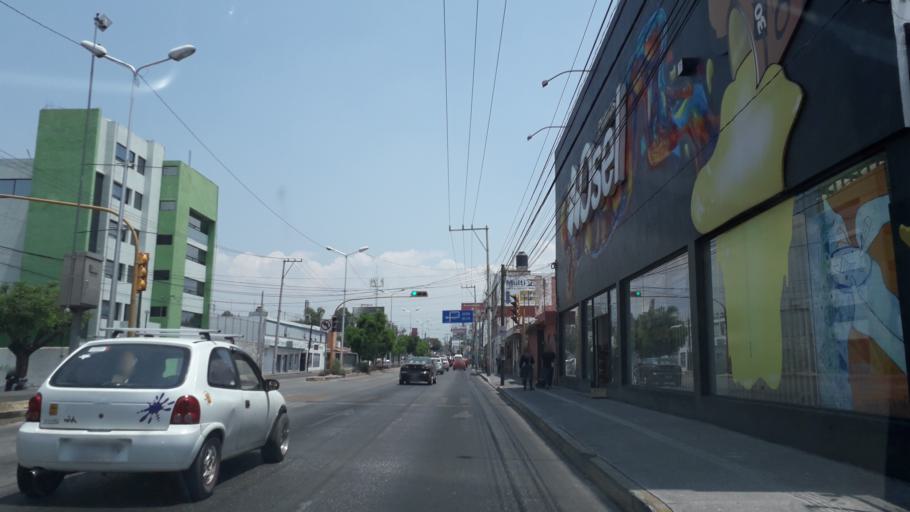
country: MX
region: Puebla
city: Puebla
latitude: 19.0233
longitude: -98.2244
